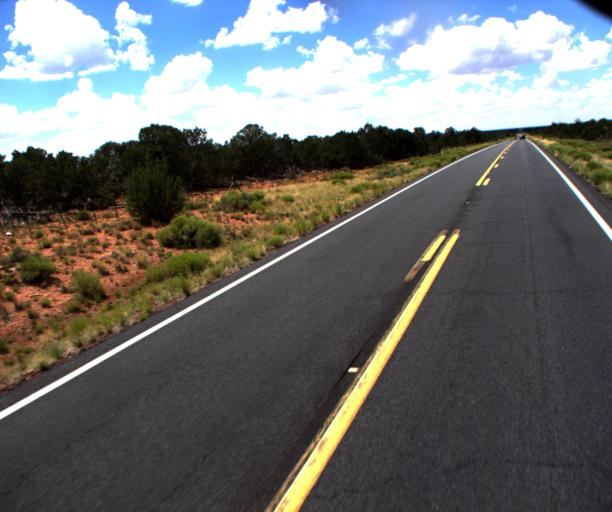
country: US
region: Arizona
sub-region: Coconino County
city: Parks
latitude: 35.5989
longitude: -112.0196
